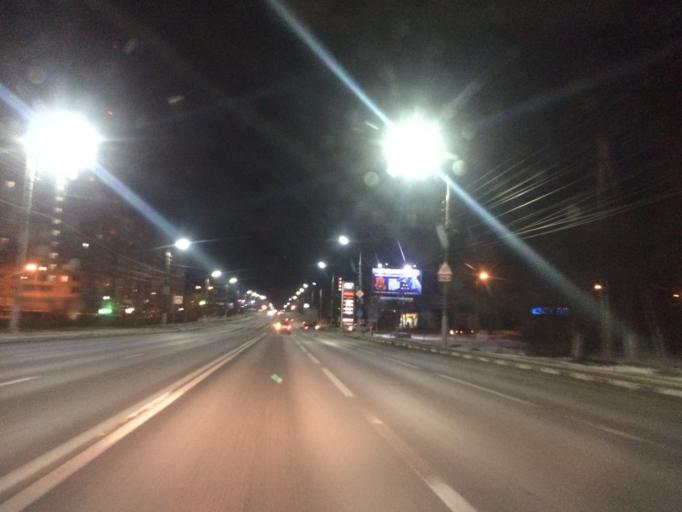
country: RU
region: Tula
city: Mendeleyevskiy
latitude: 54.1482
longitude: 37.5829
